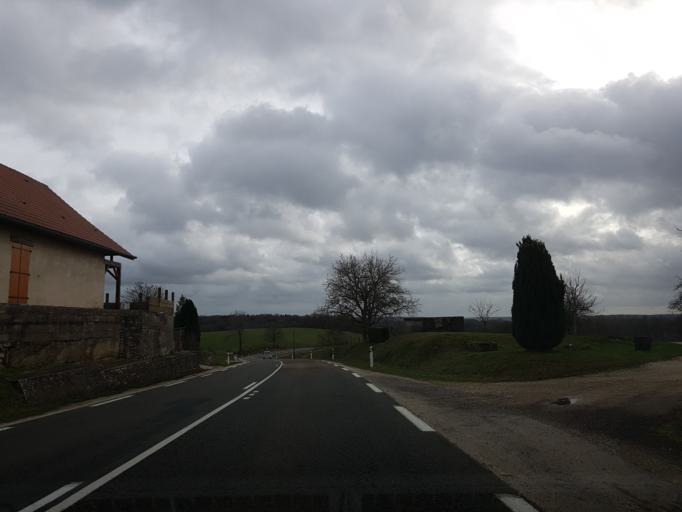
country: FR
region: Champagne-Ardenne
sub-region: Departement de la Haute-Marne
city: Chalindrey
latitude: 47.8291
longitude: 5.4774
